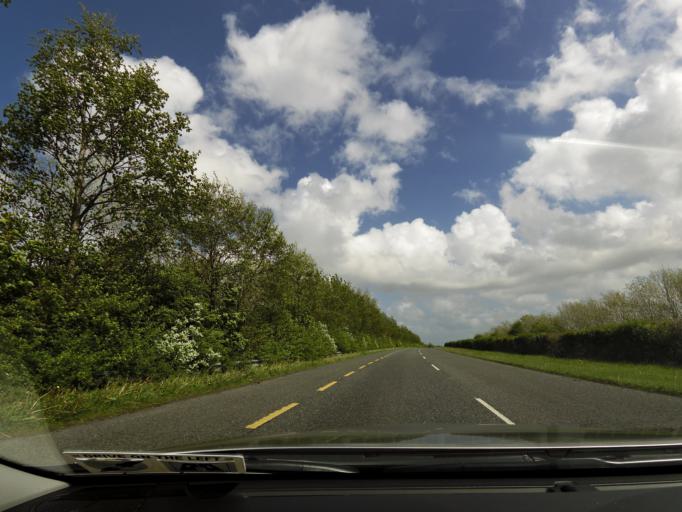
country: IE
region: Connaught
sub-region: County Galway
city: Oranmore
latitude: 53.2782
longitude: -8.9410
